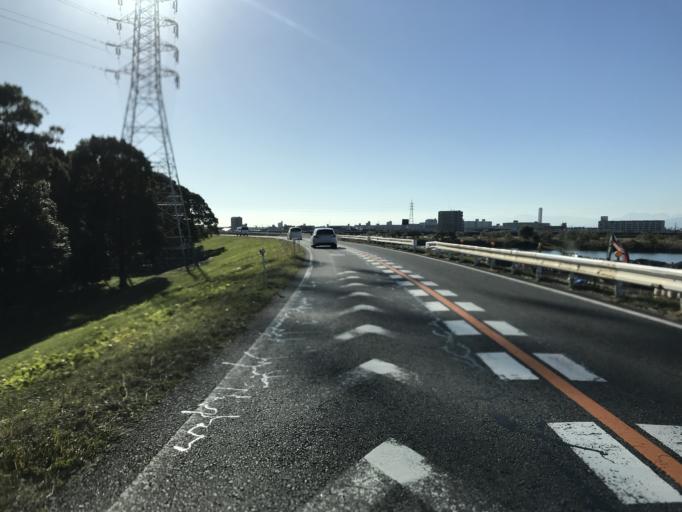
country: JP
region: Aichi
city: Kanie
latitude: 35.1503
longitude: 136.8317
